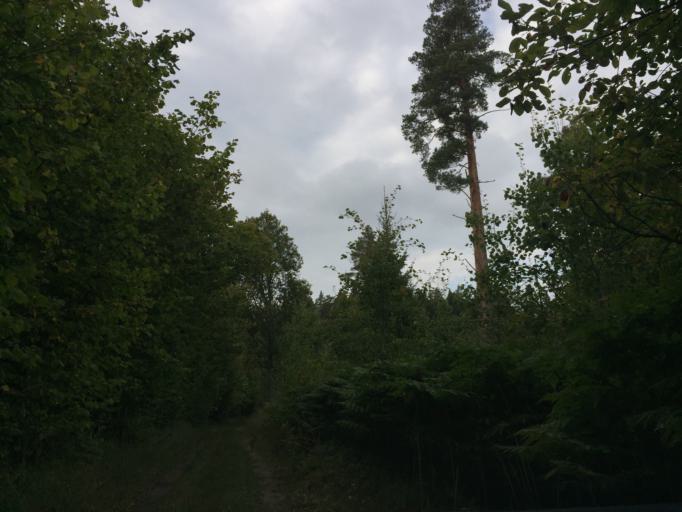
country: LV
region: Baldone
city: Baldone
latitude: 56.7709
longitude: 24.4536
